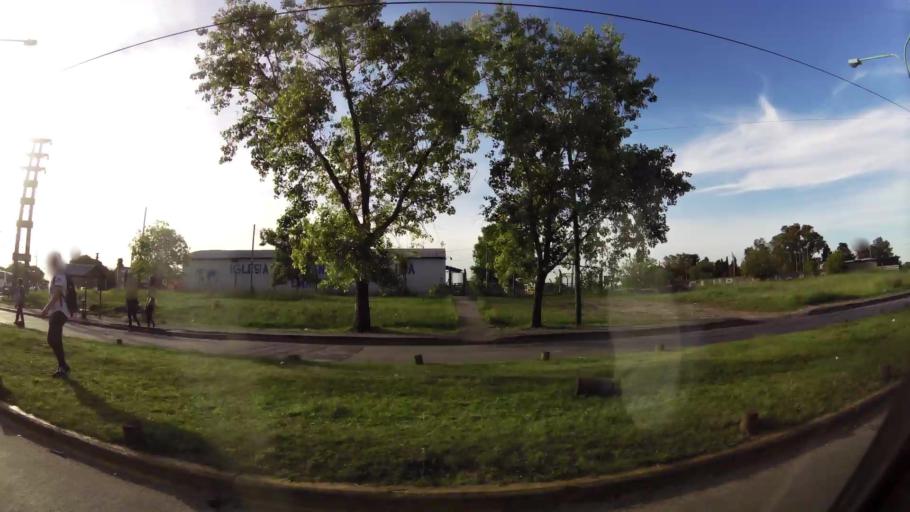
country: AR
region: Buenos Aires
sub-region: Partido de Almirante Brown
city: Adrogue
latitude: -34.8189
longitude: -58.3419
